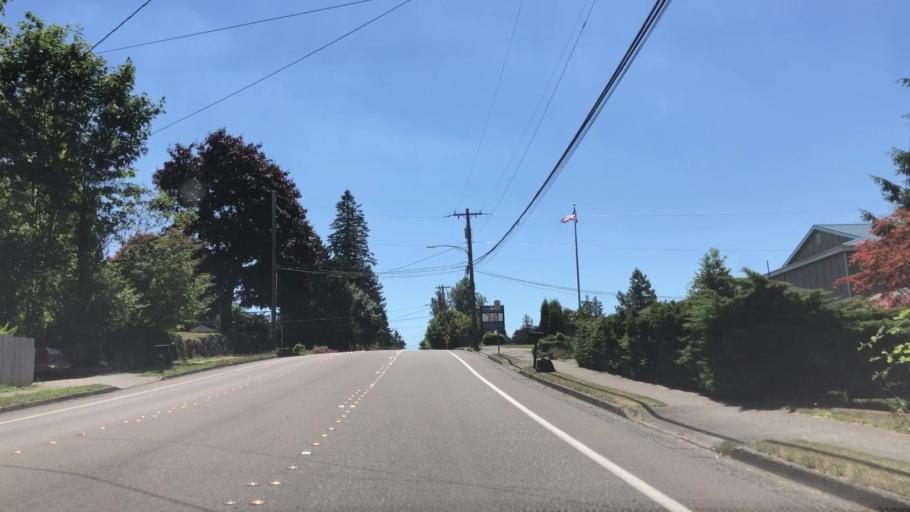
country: US
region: Washington
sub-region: Snohomish County
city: Alderwood Manor
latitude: 47.8449
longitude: -122.2926
